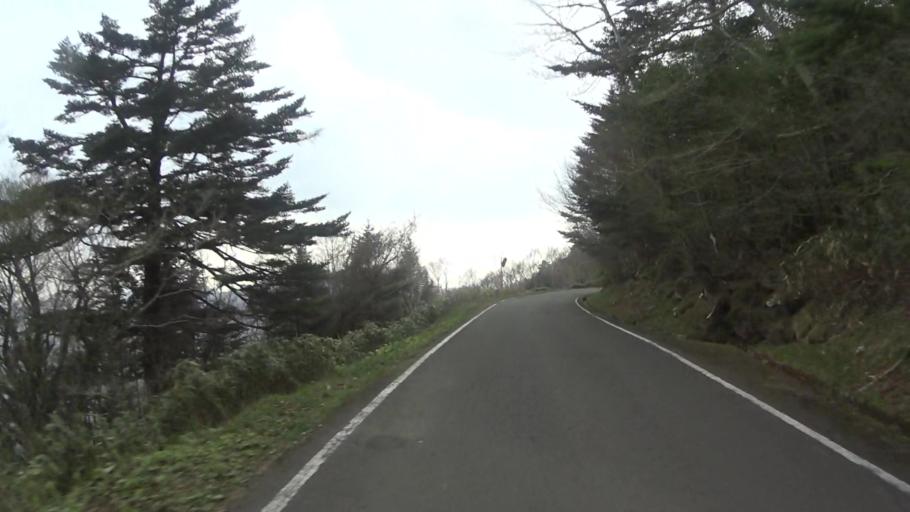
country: JP
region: Ehime
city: Saijo
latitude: 33.7842
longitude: 133.2413
